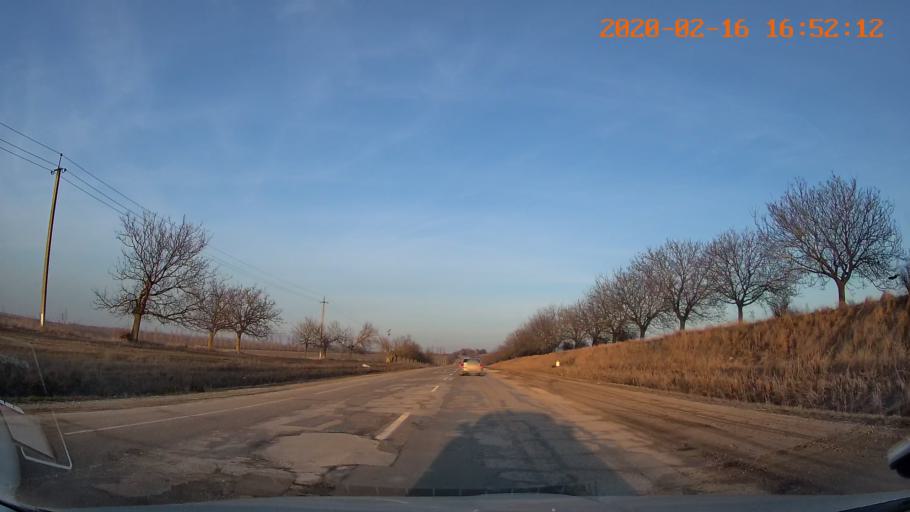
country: MD
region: Briceni
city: Briceni
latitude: 48.3111
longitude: 26.9570
